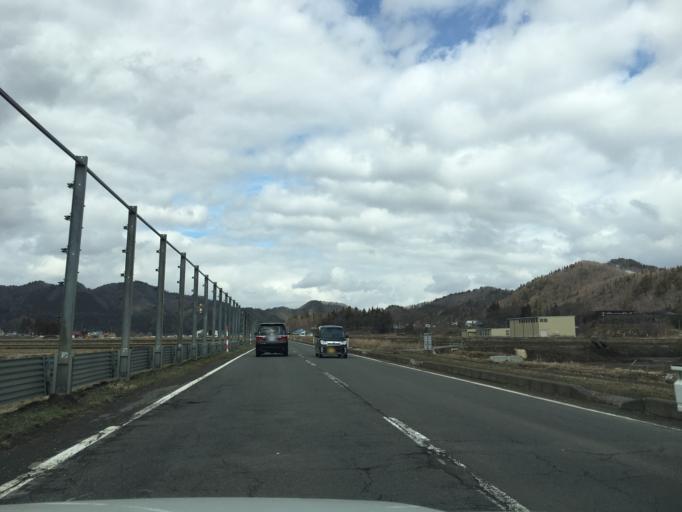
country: JP
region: Akita
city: Hanawa
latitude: 40.2307
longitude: 140.7324
